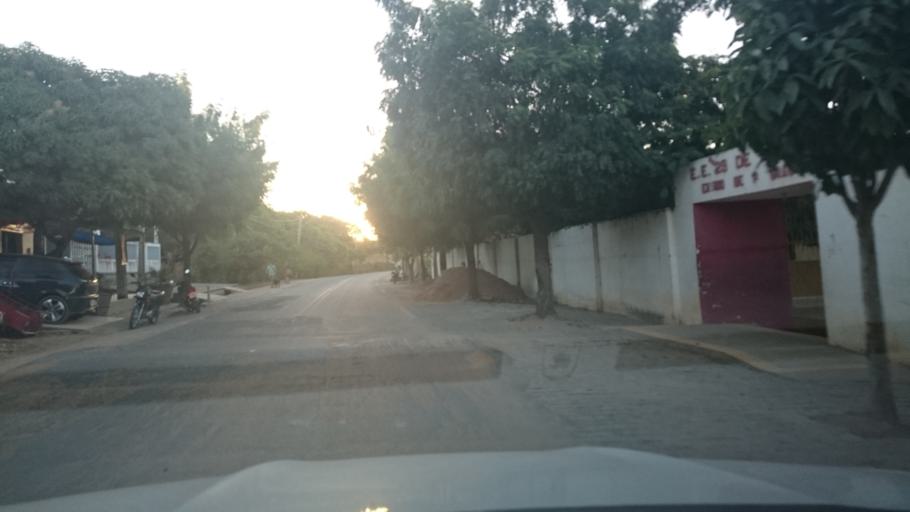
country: BR
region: Rio Grande do Norte
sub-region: Umarizal
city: Umarizal
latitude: -6.0246
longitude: -37.9913
